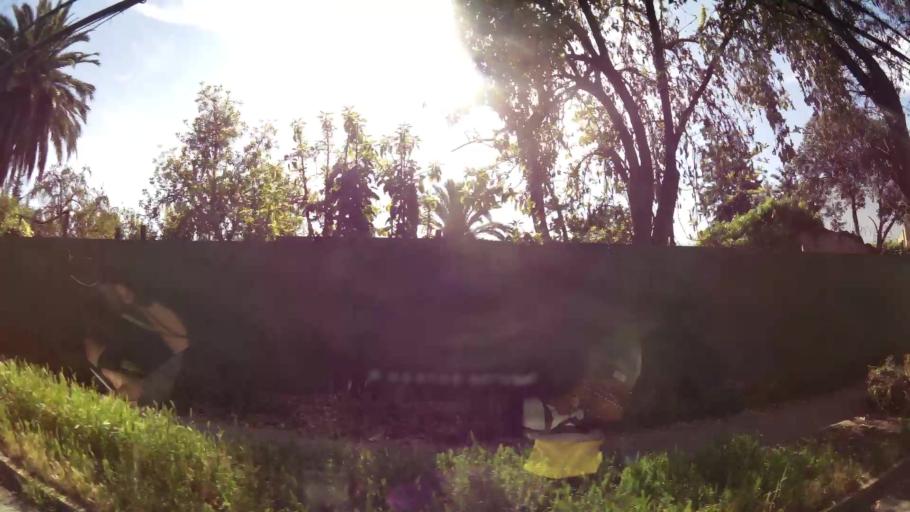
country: CL
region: Santiago Metropolitan
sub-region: Provincia de Santiago
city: Villa Presidente Frei, Nunoa, Santiago, Chile
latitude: -33.4443
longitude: -70.5316
